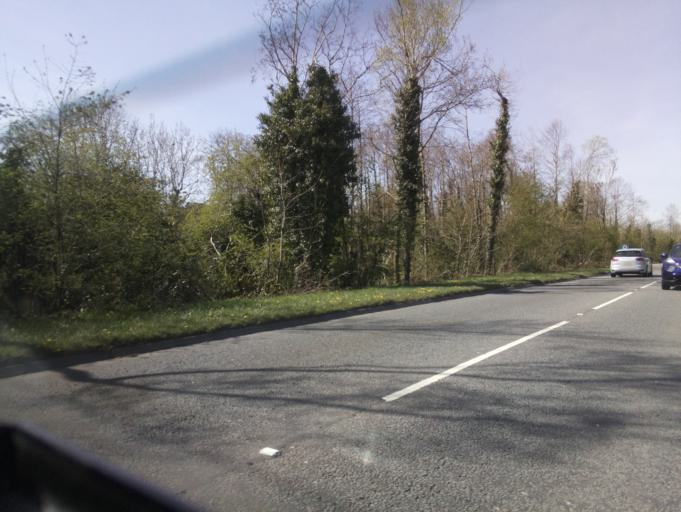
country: GB
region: Wales
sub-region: Rhondda Cynon Taf
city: Aberdare
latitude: 51.7231
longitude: -3.4535
